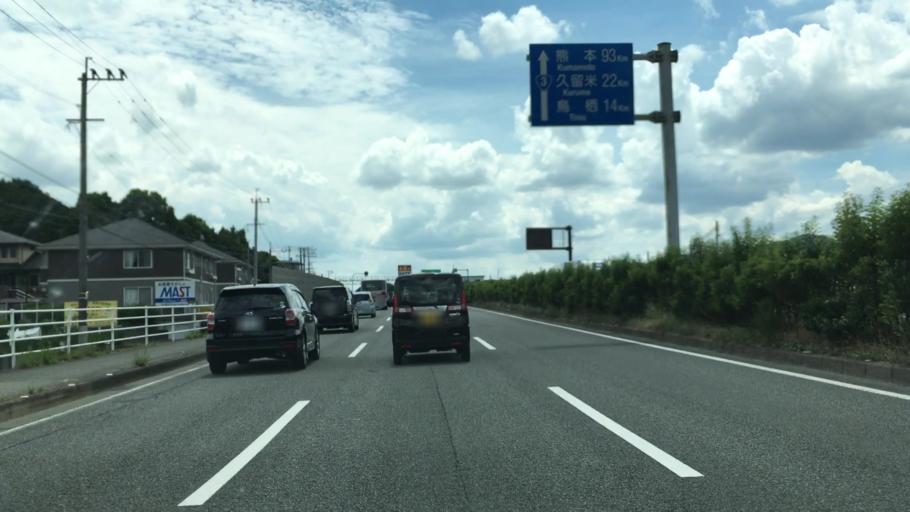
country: JP
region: Fukuoka
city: Chikushino-shi
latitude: 33.4919
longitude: 130.5354
